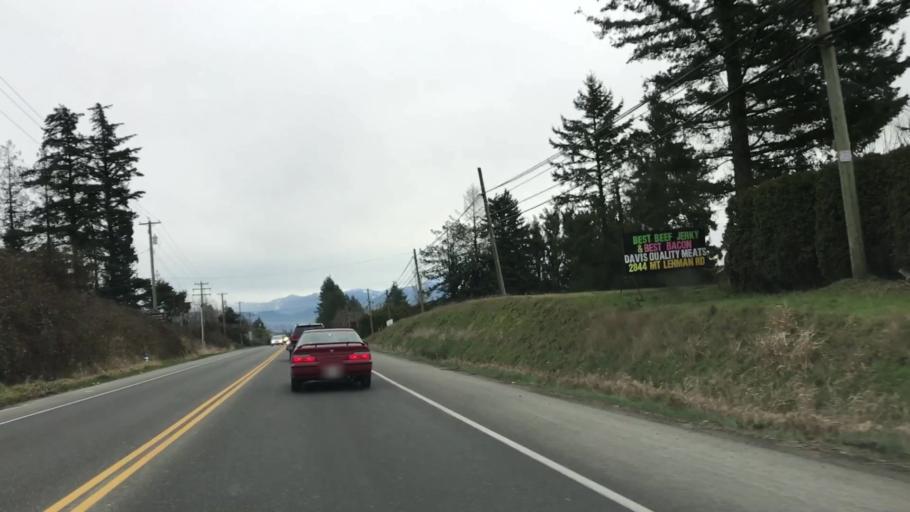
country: CA
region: British Columbia
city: Aldergrove
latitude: 49.0574
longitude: -122.3995
